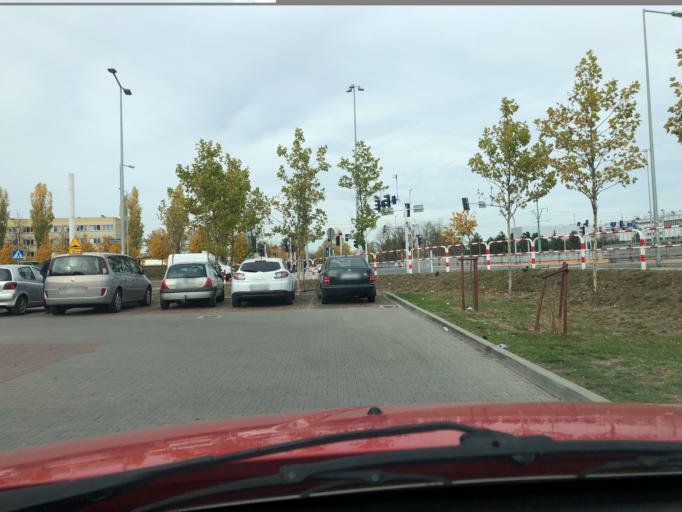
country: PL
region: Greater Poland Voivodeship
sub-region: Powiat poznanski
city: Plewiska
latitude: 52.3894
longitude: 16.8542
